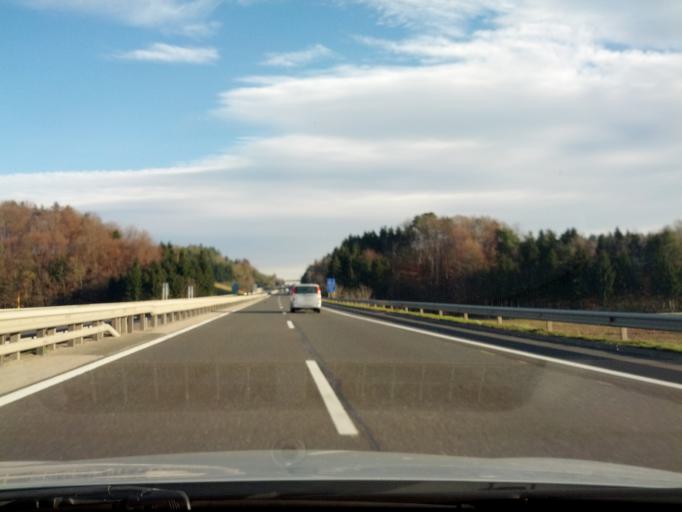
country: SI
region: Oplotnica
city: Oplotnica
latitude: 46.3508
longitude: 15.4912
